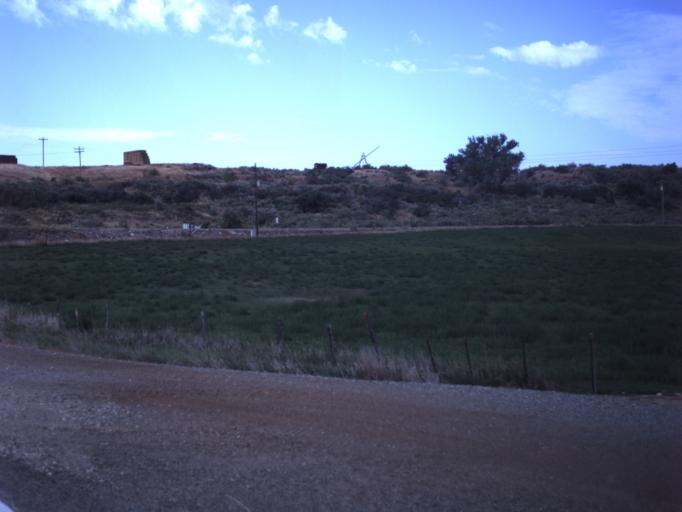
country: US
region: Utah
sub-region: Uintah County
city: Naples
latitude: 40.4069
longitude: -109.3414
